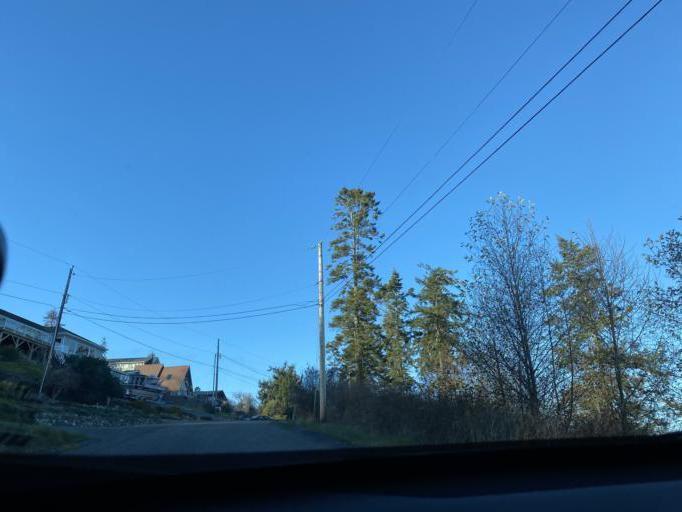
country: US
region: Washington
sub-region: Island County
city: Camano
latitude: 48.1292
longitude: -122.5644
